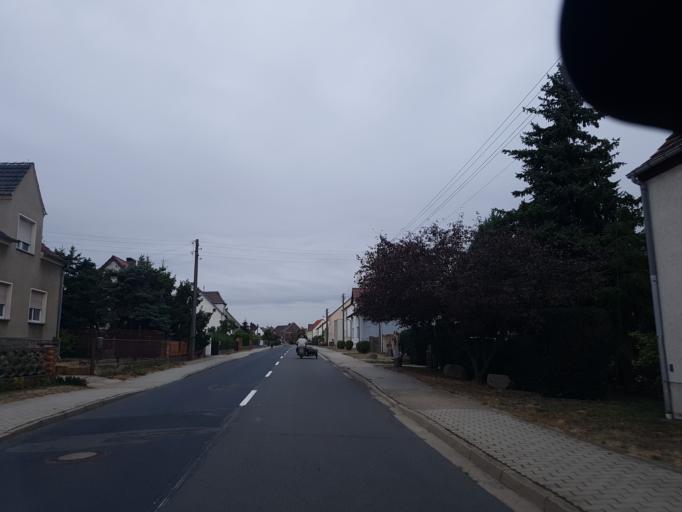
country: DE
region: Saxony-Anhalt
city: Prettin
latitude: 51.6575
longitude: 12.9388
